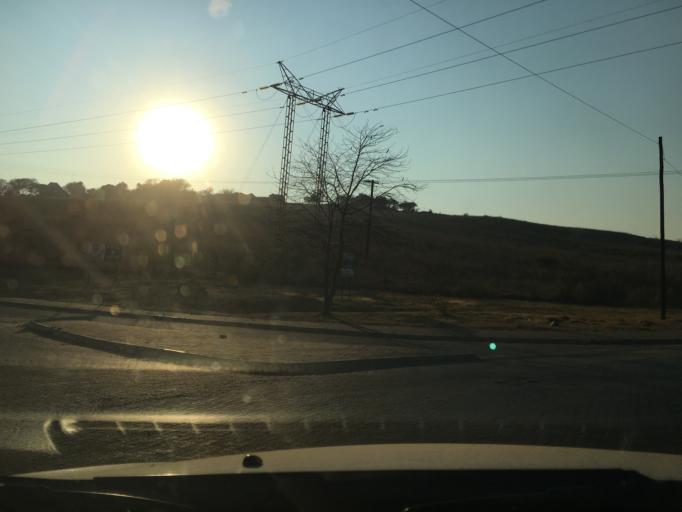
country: ZA
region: Gauteng
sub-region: West Rand District Municipality
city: Muldersdriseloop
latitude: -25.9913
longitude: 27.8463
